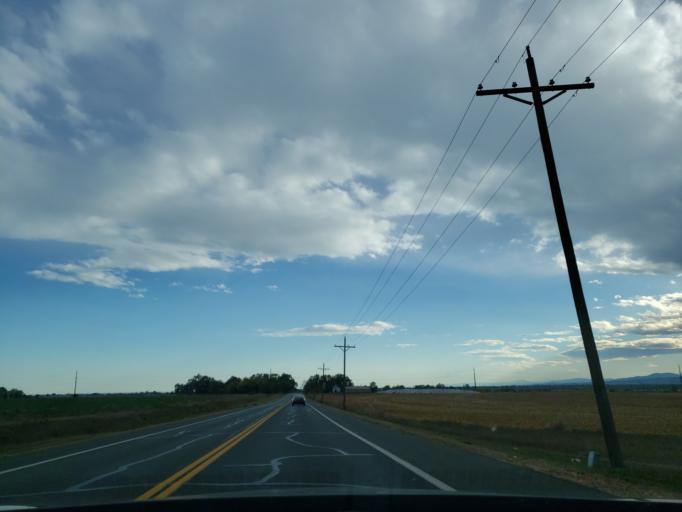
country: US
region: Colorado
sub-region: Larimer County
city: Fort Collins
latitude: 40.6082
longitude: -105.0293
